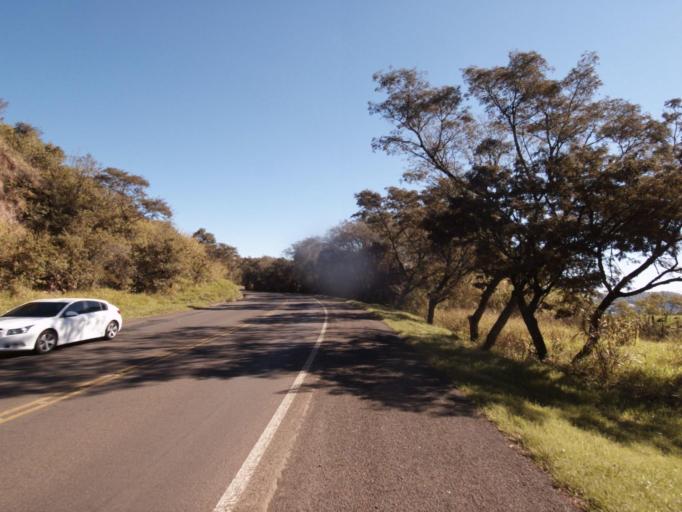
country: BR
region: Rio Grande do Sul
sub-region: Frederico Westphalen
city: Frederico Westphalen
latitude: -26.7931
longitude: -53.4517
